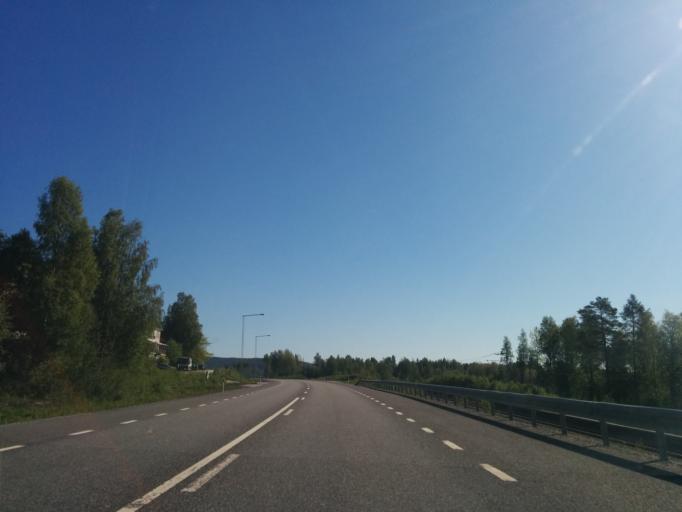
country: SE
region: Vaesternorrland
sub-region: Kramfors Kommun
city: Kramfors
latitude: 62.8315
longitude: 17.8677
